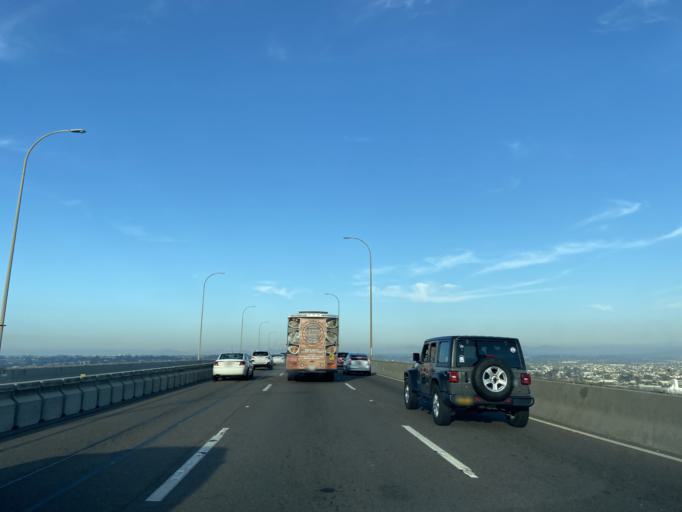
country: US
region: California
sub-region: San Diego County
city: San Diego
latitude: 32.6903
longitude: -117.1519
